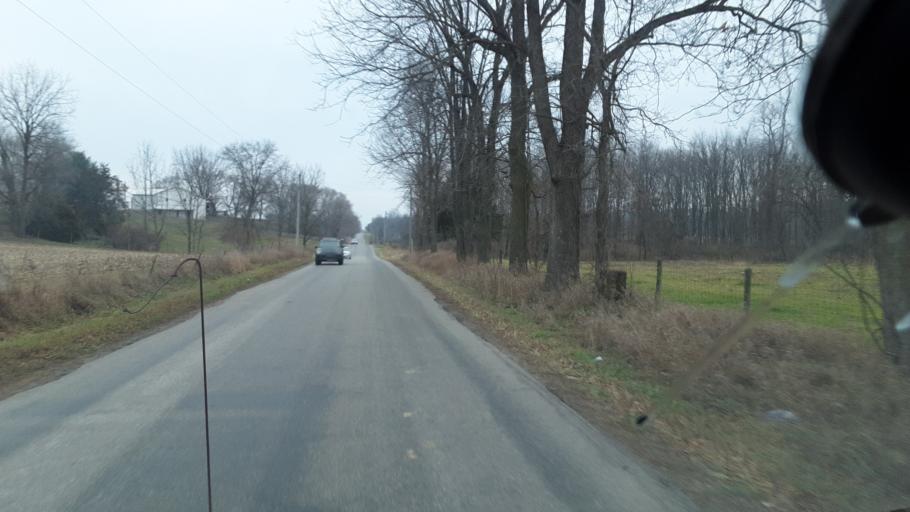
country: US
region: Michigan
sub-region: Saint Joseph County
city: White Pigeon
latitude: 41.7208
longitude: -85.6208
